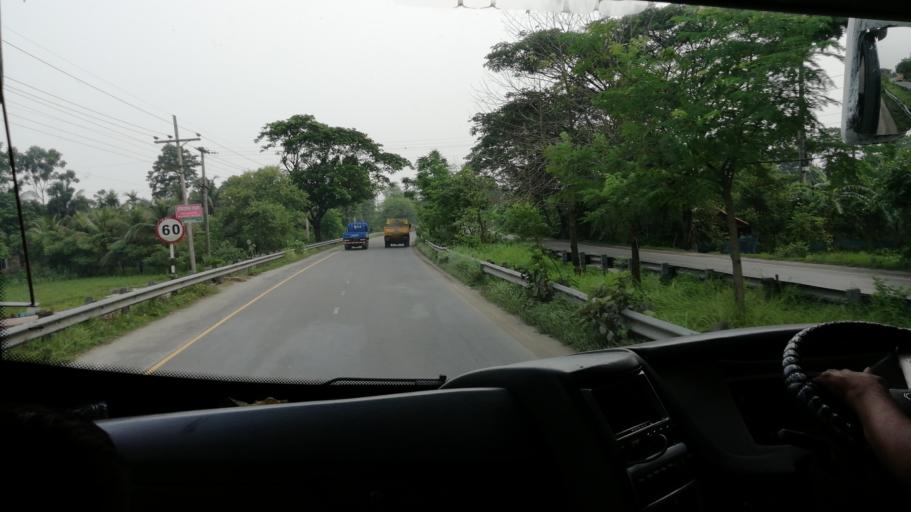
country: BD
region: Khulna
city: Khulna
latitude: 22.7883
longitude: 89.5339
